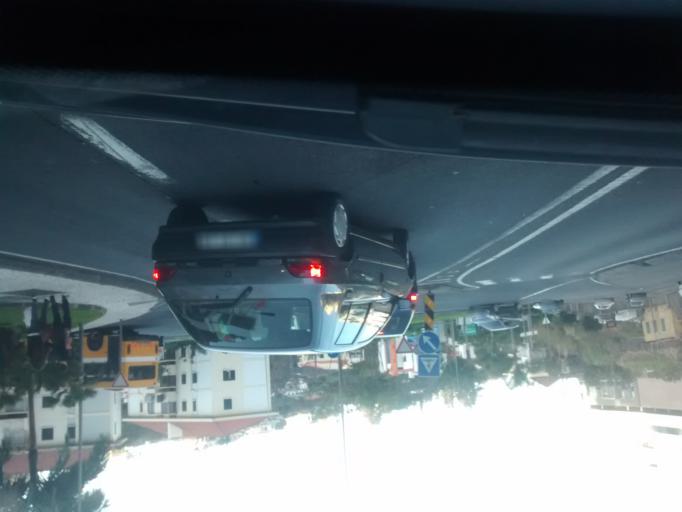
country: PT
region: Madeira
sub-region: Funchal
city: Nossa Senhora do Monte
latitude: 32.6602
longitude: -16.9193
